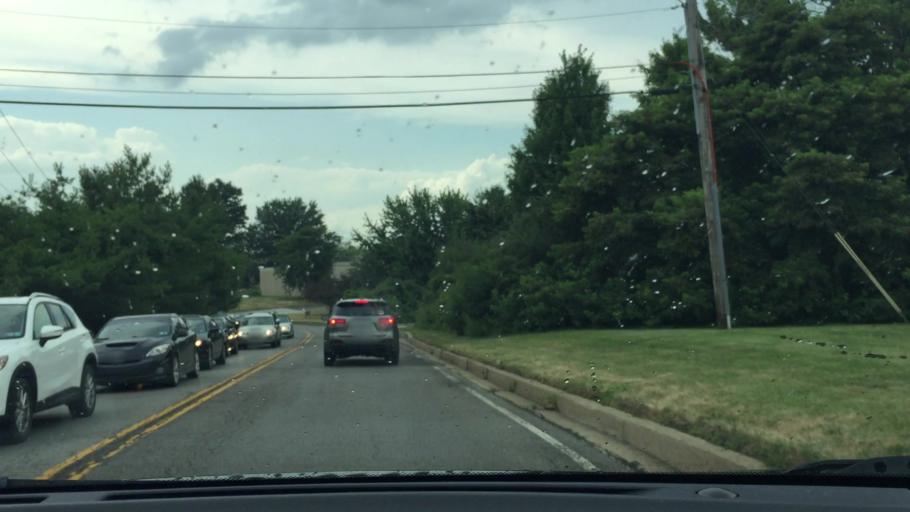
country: US
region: Pennsylvania
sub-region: Butler County
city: Cranberry Township
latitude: 40.6682
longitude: -80.1040
